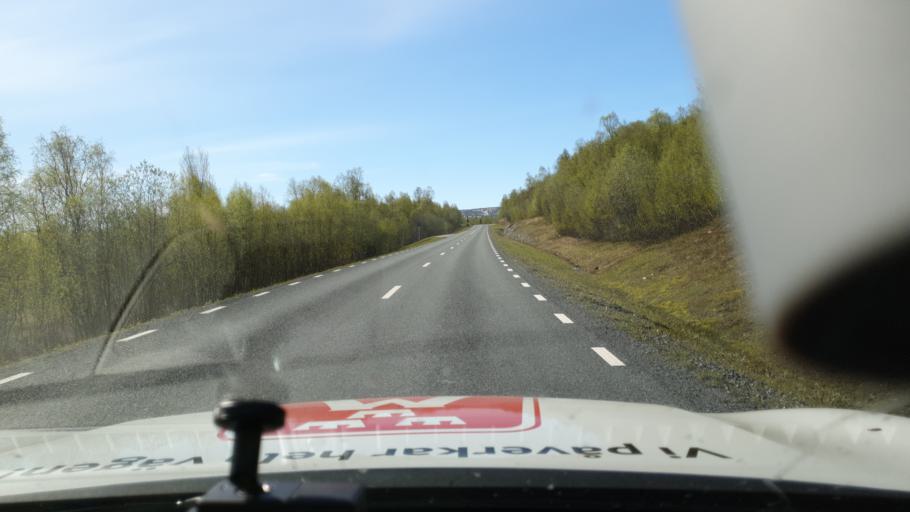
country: NO
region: Nordland
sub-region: Rana
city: Mo i Rana
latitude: 65.7673
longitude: 15.1133
